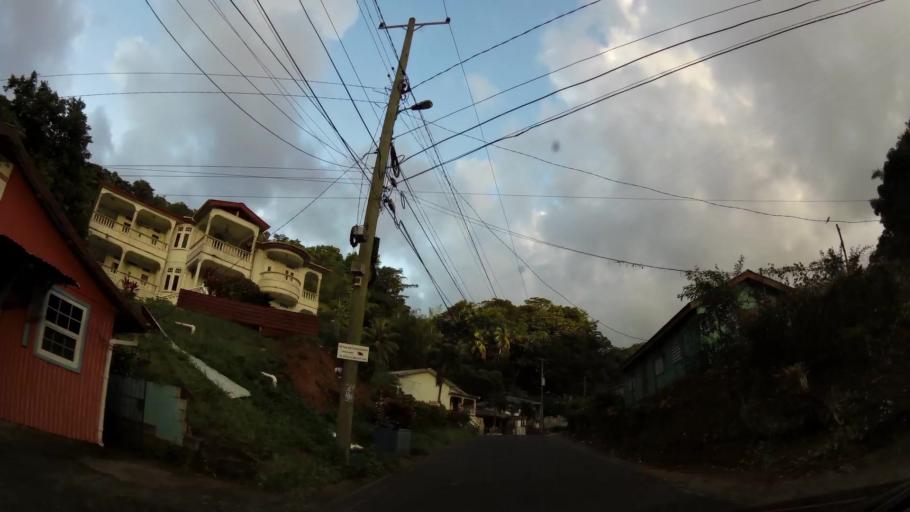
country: DM
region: Saint John
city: Portsmouth
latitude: 15.5852
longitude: -61.4123
